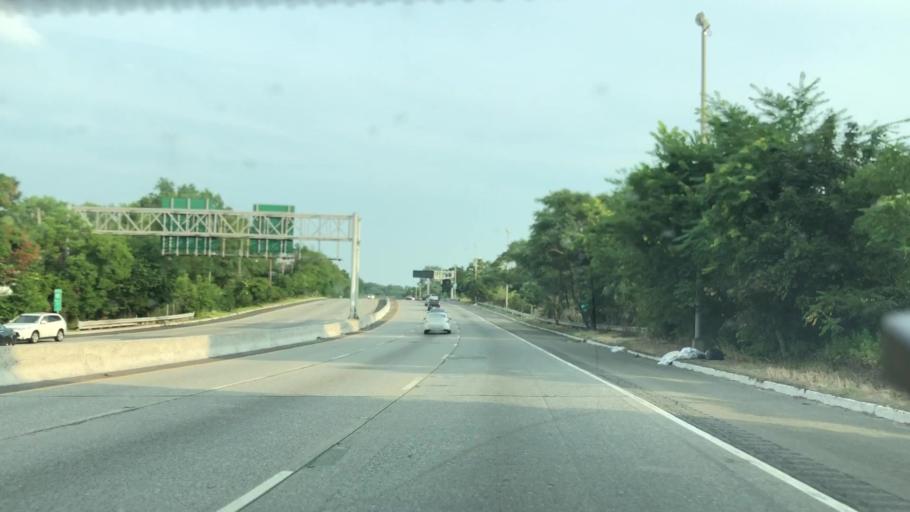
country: US
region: New Jersey
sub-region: Bergen County
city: Wallington
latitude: 40.8366
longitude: -74.1251
